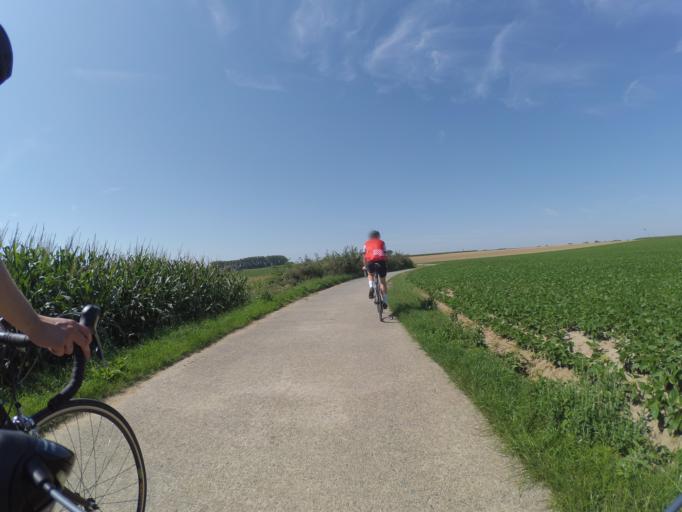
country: BE
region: Flanders
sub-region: Provincie Oost-Vlaanderen
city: Kruishoutem
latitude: 50.8532
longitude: 3.5345
